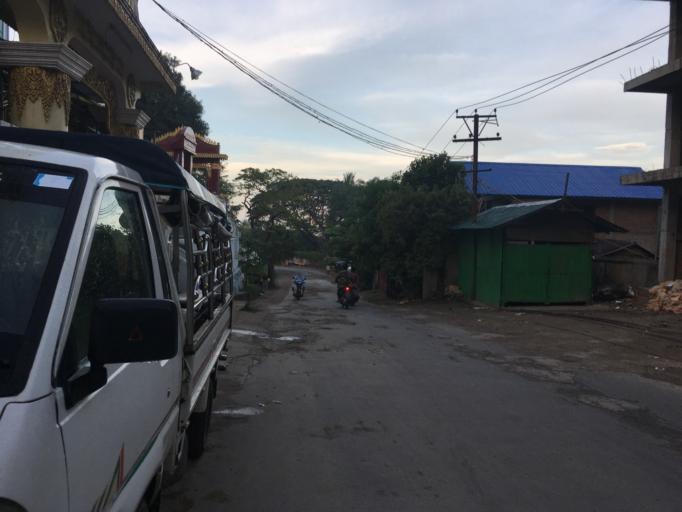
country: MM
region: Mon
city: Mawlamyine
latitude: 16.4868
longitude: 97.6275
